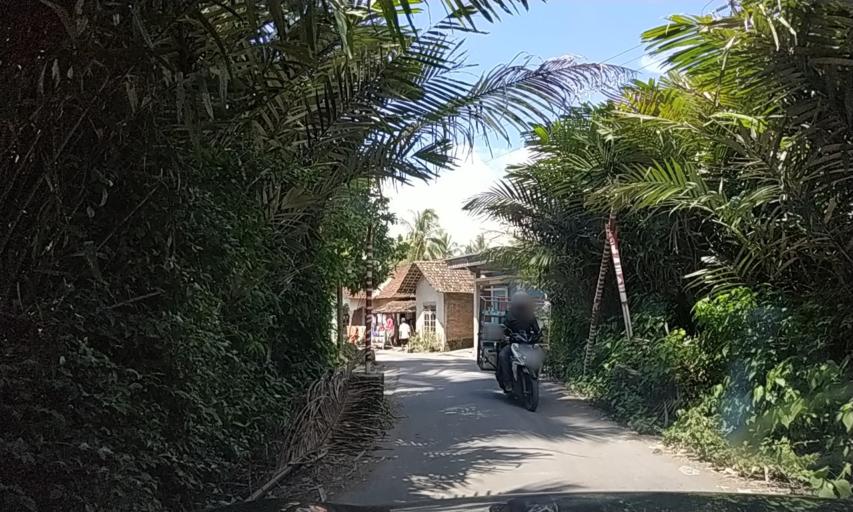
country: ID
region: Central Java
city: Muntilan
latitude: -7.6006
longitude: 110.3545
